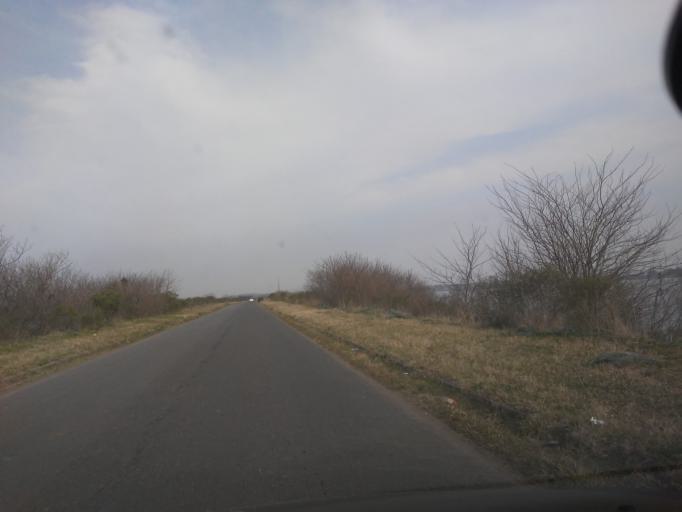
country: AR
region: Buenos Aires
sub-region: Partido de Marcos Paz
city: Marcos Paz
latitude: -34.6810
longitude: -58.8597
